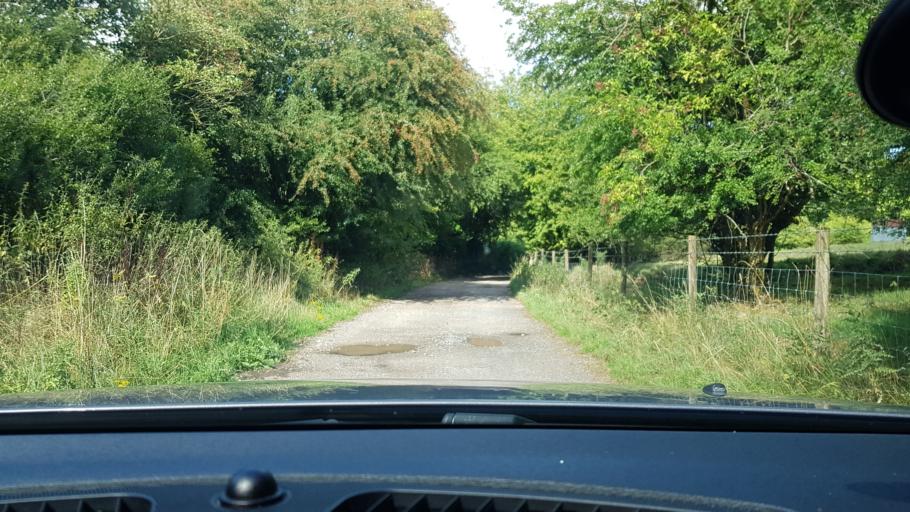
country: GB
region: England
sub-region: Wiltshire
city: Mildenhall
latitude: 51.4043
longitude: -1.6920
